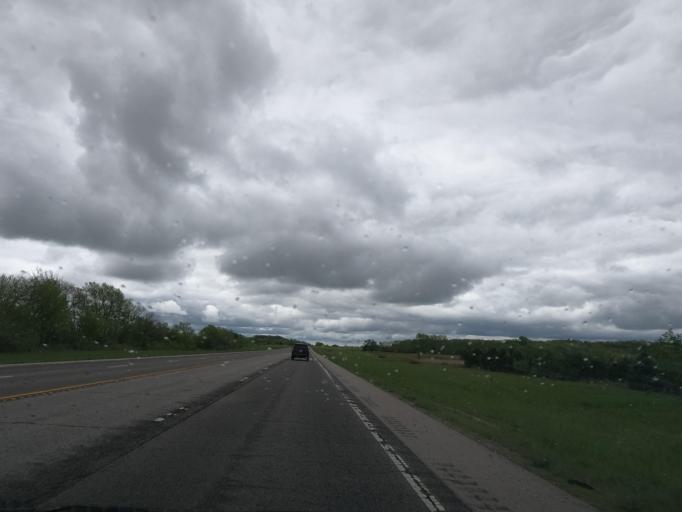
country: US
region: Kansas
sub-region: Montgomery County
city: Cherryvale
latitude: 37.3470
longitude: -95.4878
